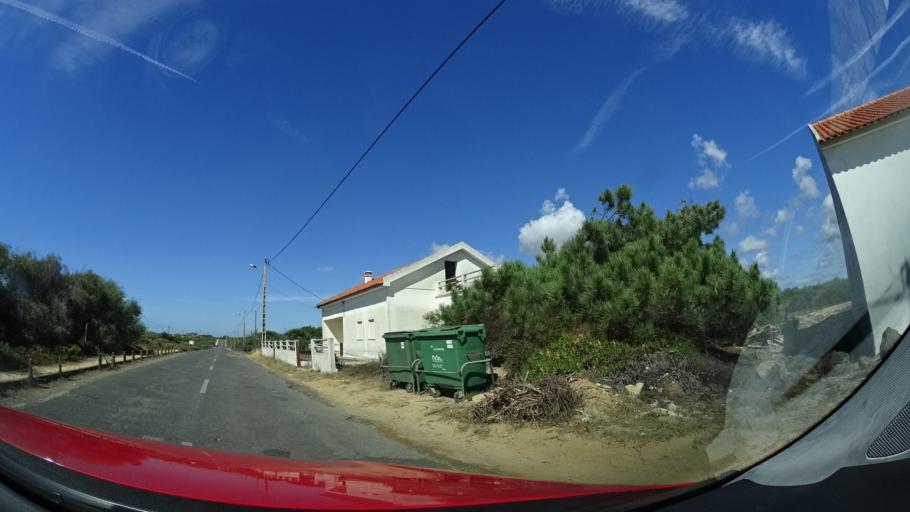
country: PT
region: Beja
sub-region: Odemira
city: Sao Teotonio
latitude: 37.5289
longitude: -8.7843
